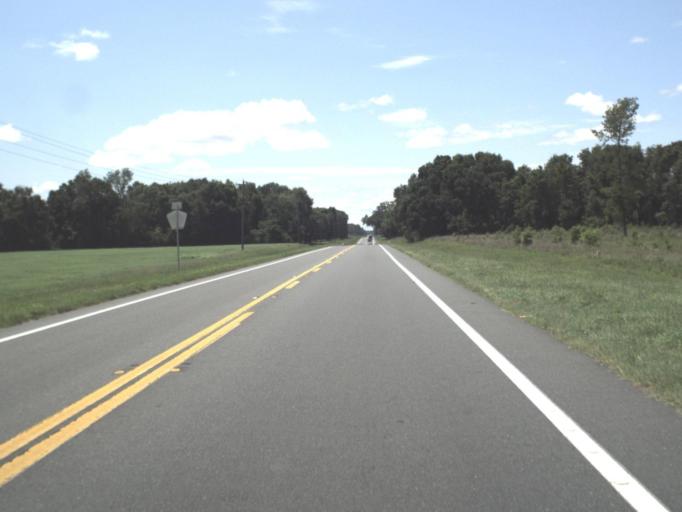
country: US
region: Florida
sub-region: Lafayette County
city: Mayo
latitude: 30.0984
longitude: -83.2380
